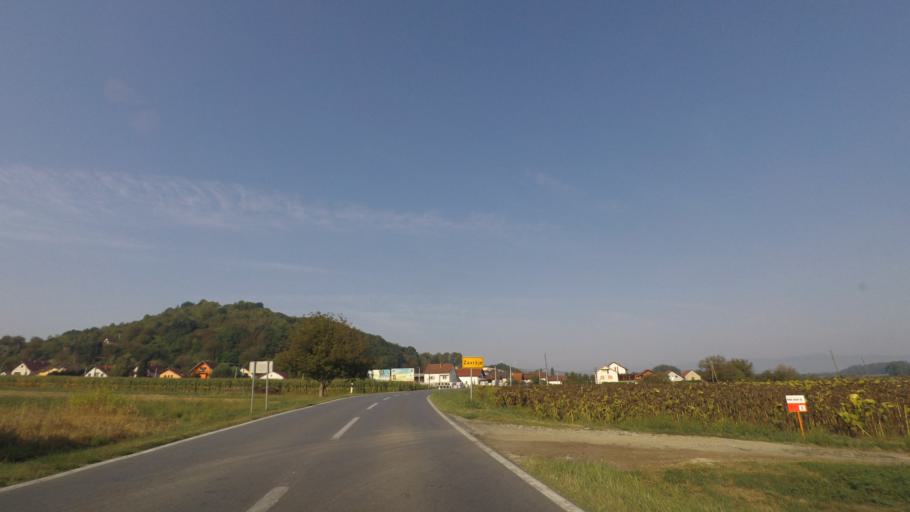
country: HR
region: Pozesko-Slavonska
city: Pozega
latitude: 45.3266
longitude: 17.6353
